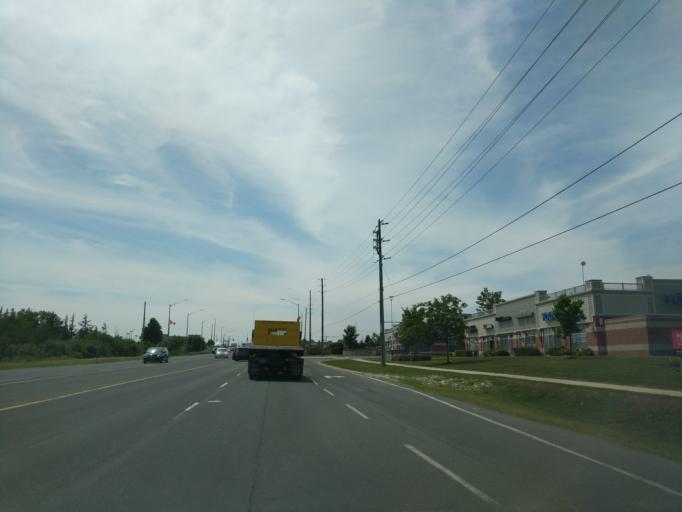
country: CA
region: Ontario
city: Vaughan
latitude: 43.8619
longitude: -79.4838
